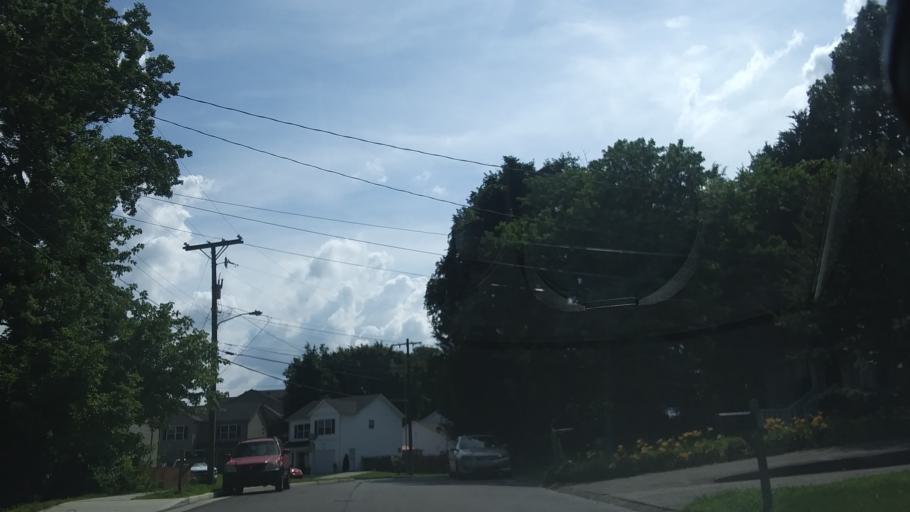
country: US
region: Tennessee
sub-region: Rutherford County
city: La Vergne
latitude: 36.0804
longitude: -86.6387
